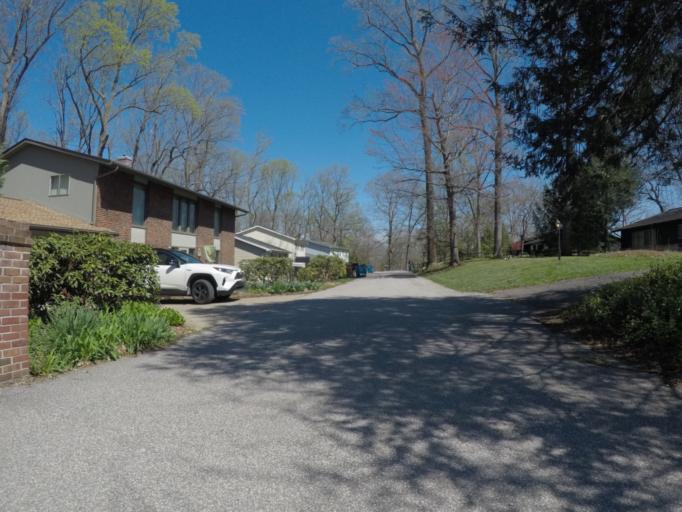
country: US
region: West Virginia
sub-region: Cabell County
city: Pea Ridge
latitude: 38.4132
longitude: -82.3177
